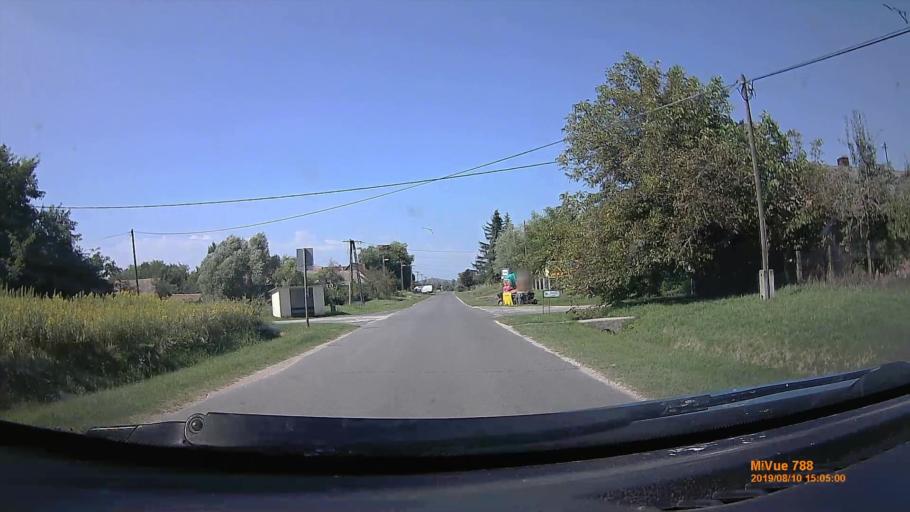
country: HU
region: Somogy
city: Lengyeltoti
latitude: 46.6778
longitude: 17.5656
